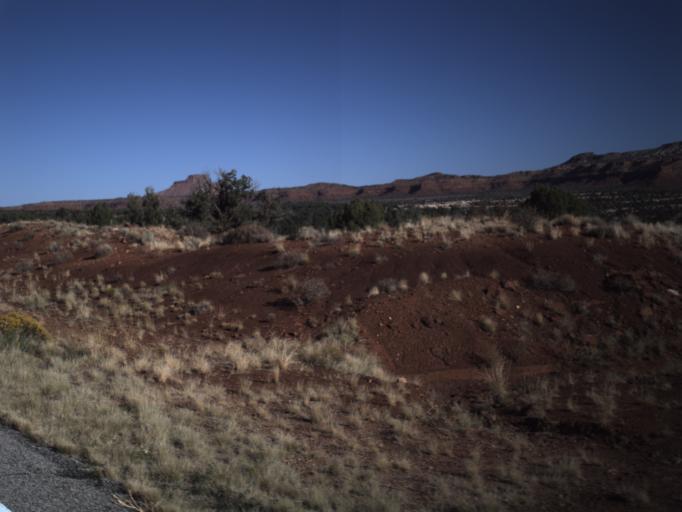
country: US
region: Utah
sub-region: San Juan County
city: Blanding
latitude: 37.6372
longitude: -110.1594
